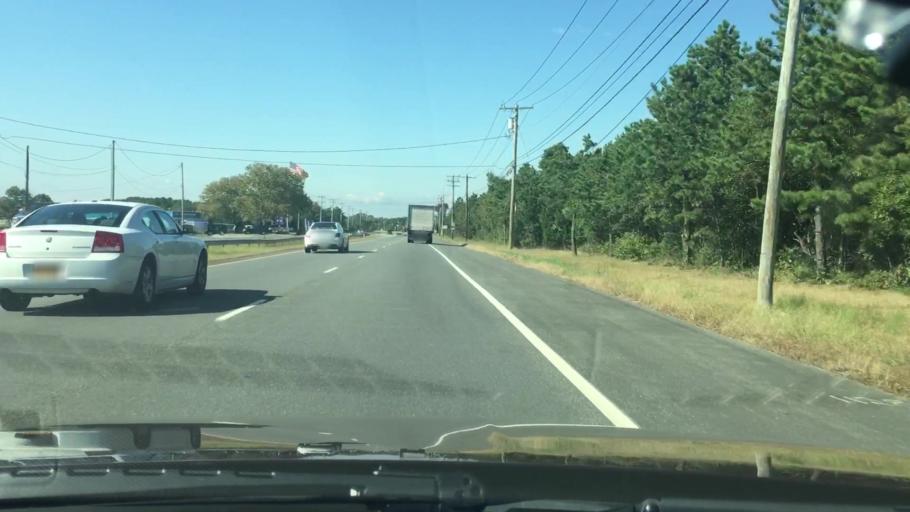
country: US
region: New York
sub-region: Suffolk County
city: Holbrook
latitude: 40.7772
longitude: -73.0721
